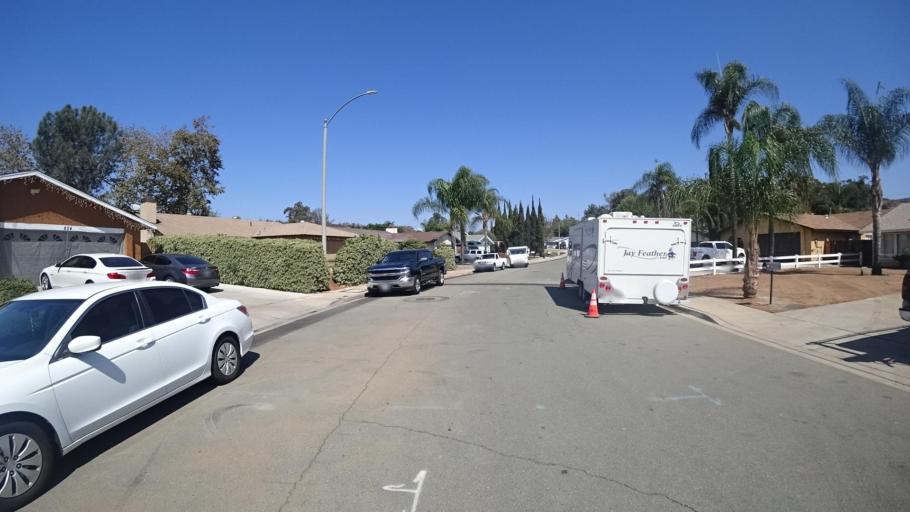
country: US
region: California
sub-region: San Diego County
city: Granite Hills
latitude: 32.8057
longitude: -116.9197
